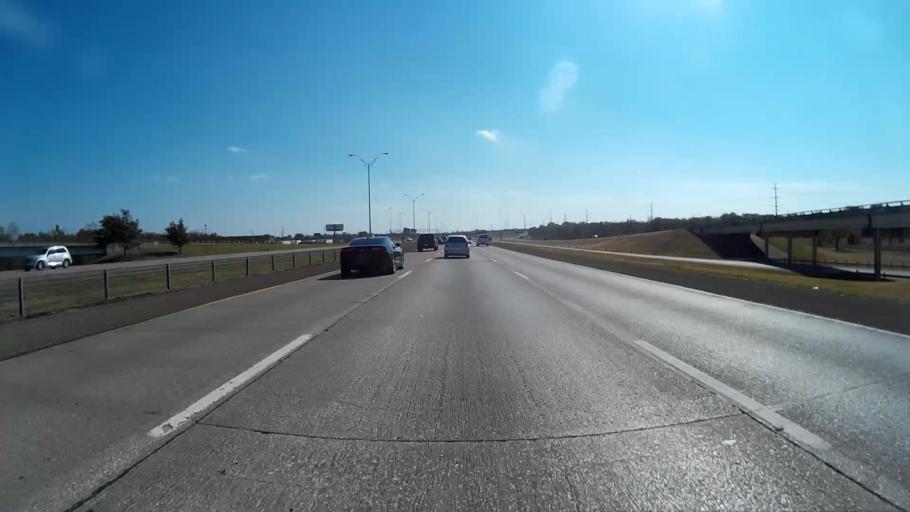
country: US
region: Texas
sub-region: Dallas County
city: Hutchins
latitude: 32.7095
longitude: -96.7557
